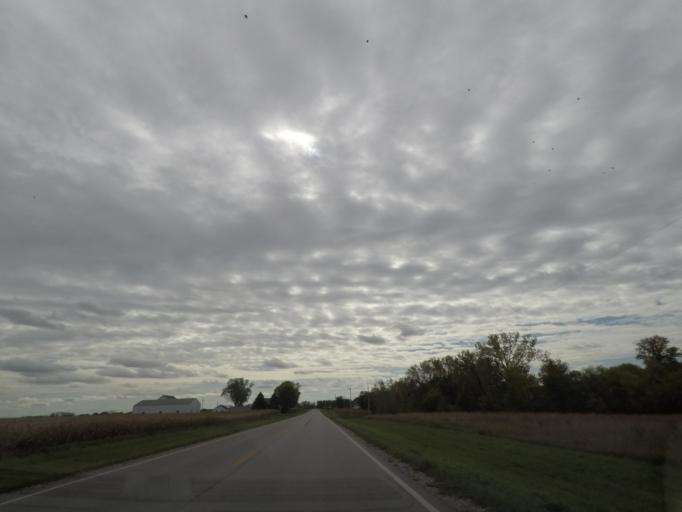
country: US
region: Iowa
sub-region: Story County
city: Huxley
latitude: 41.8450
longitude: -93.5316
